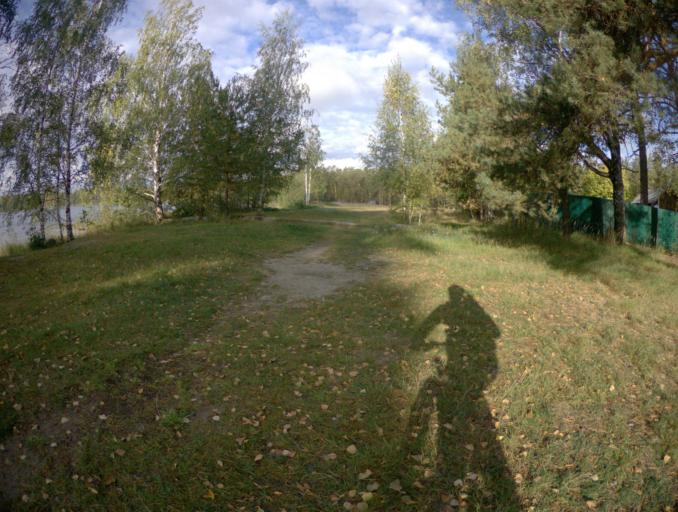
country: RU
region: Moskovskaya
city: Misheronskiy
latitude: 55.6368
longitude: 39.7420
